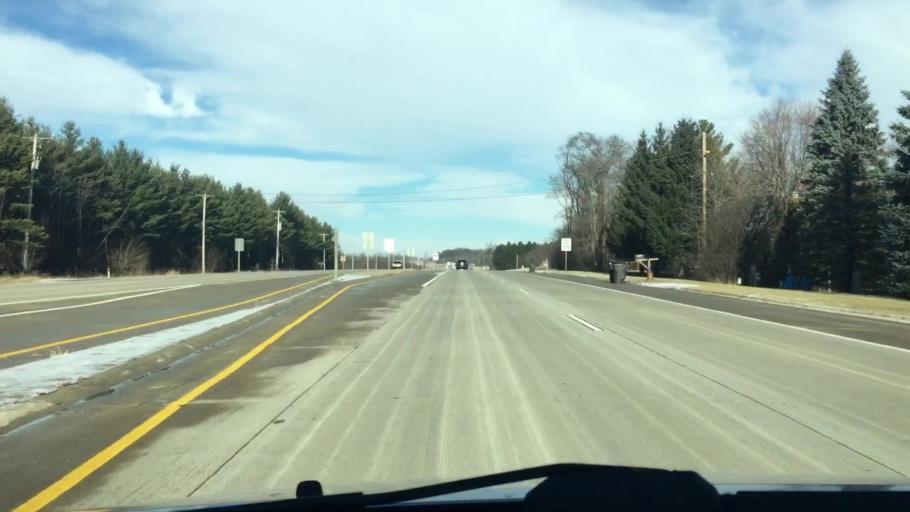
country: US
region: Wisconsin
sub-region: Waukesha County
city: Mukwonago
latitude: 42.8876
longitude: -88.3435
